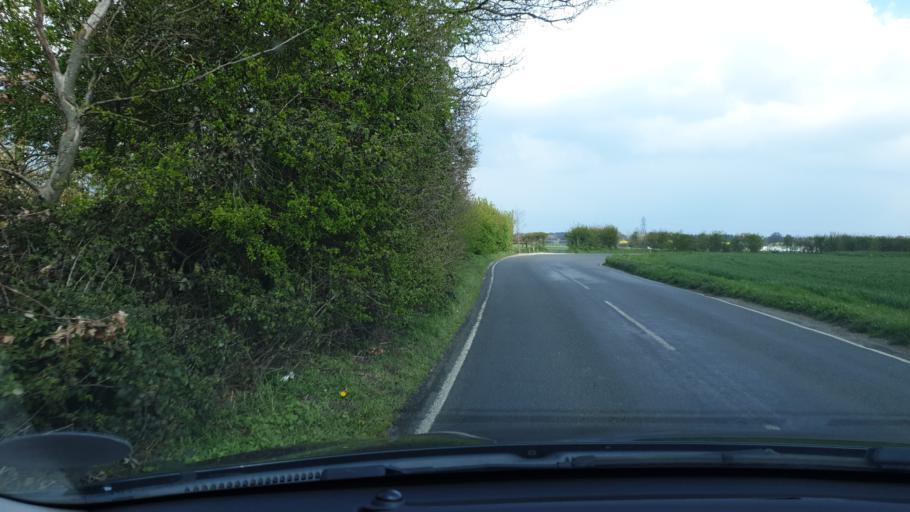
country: GB
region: England
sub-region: Essex
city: Great Bentley
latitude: 51.8696
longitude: 1.1038
